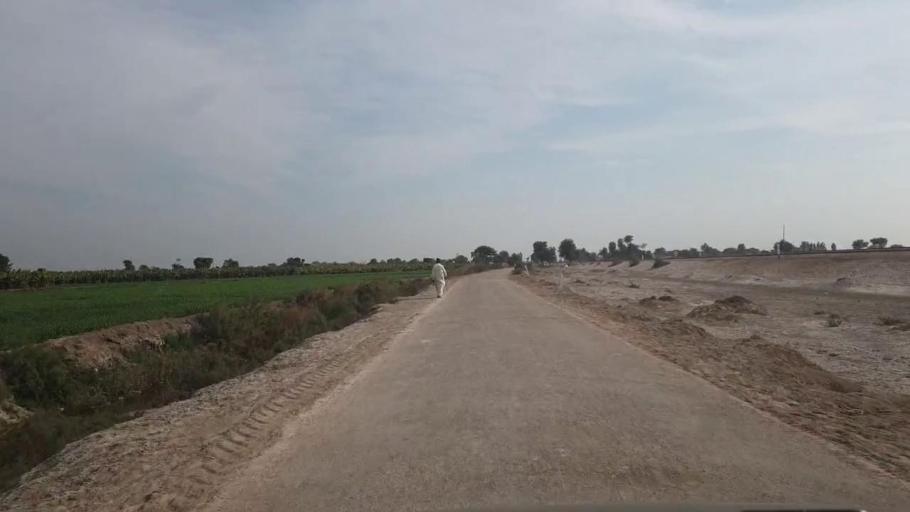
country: PK
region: Sindh
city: Shahpur Chakar
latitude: 26.0854
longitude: 68.4889
